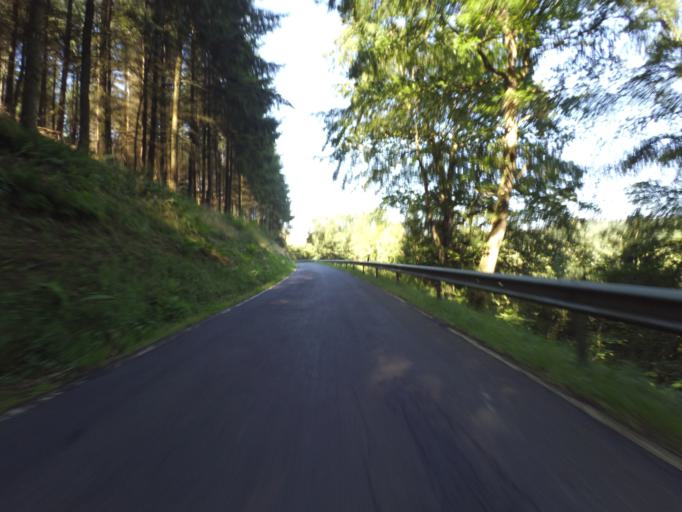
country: DE
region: Rheinland-Pfalz
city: Schladt
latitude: 50.0403
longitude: 6.8488
